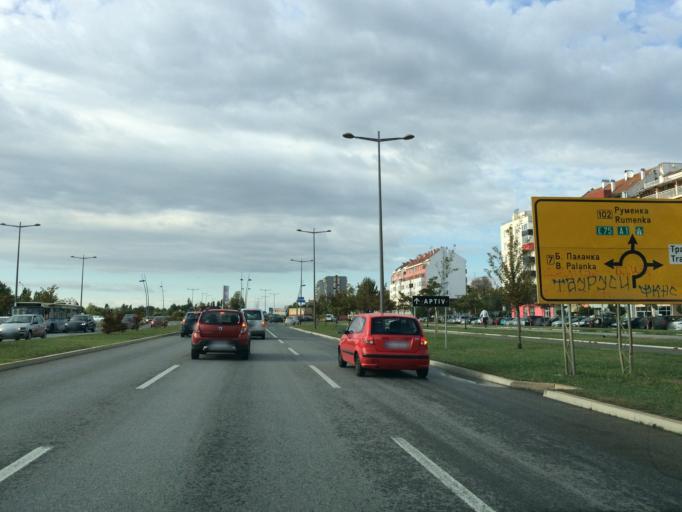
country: RS
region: Autonomna Pokrajina Vojvodina
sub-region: Juznobacki Okrug
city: Novi Sad
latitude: 45.2590
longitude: 19.8096
